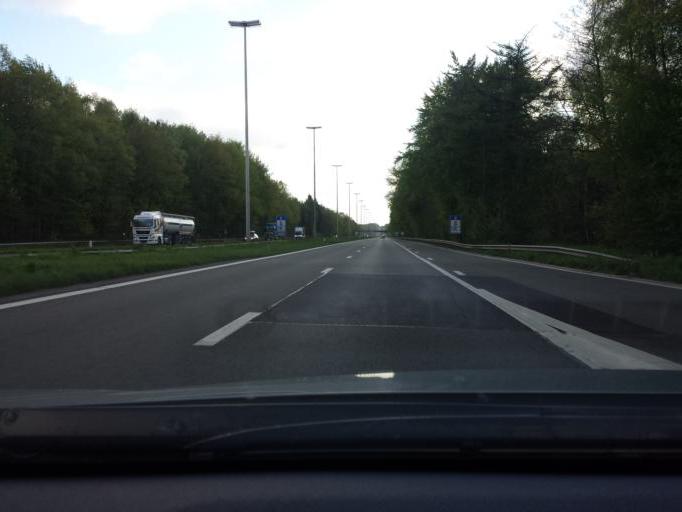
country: BE
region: Wallonia
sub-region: Province de Liege
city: Raeren
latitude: 50.7144
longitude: 6.1117
